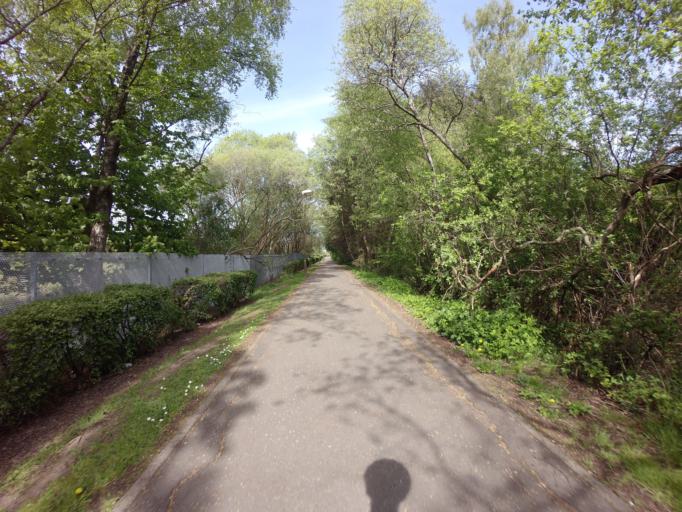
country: GB
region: Scotland
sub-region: West Lothian
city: Livingston
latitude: 55.9076
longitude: -3.5323
